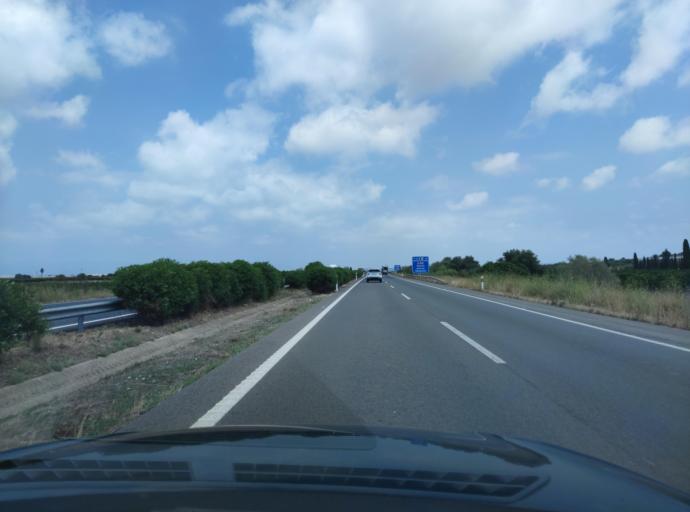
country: ES
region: Valencia
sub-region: Provincia de Castello
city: Vinaros
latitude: 40.5093
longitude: 0.4155
